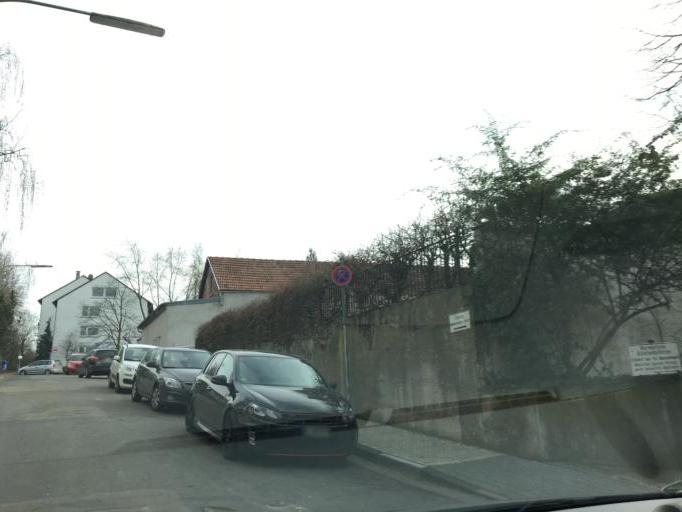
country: DE
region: Hesse
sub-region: Regierungsbezirk Darmstadt
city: Bad Vilbel
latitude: 50.1726
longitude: 8.6981
